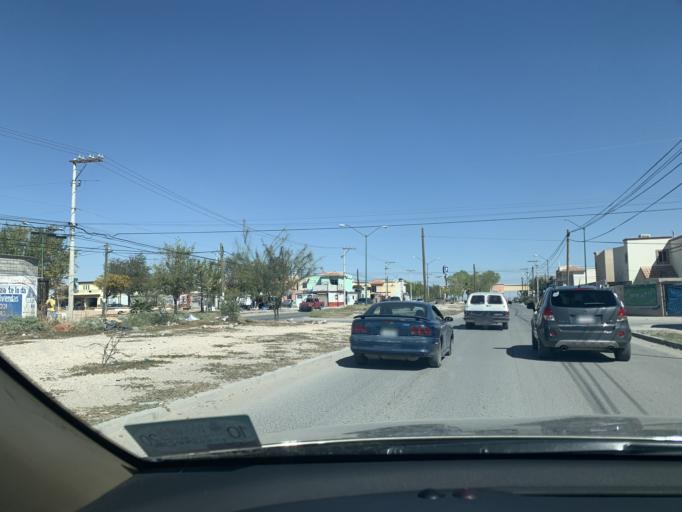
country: US
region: Texas
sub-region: El Paso County
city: Socorro Mission Number 1 Colonia
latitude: 31.6030
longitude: -106.3548
